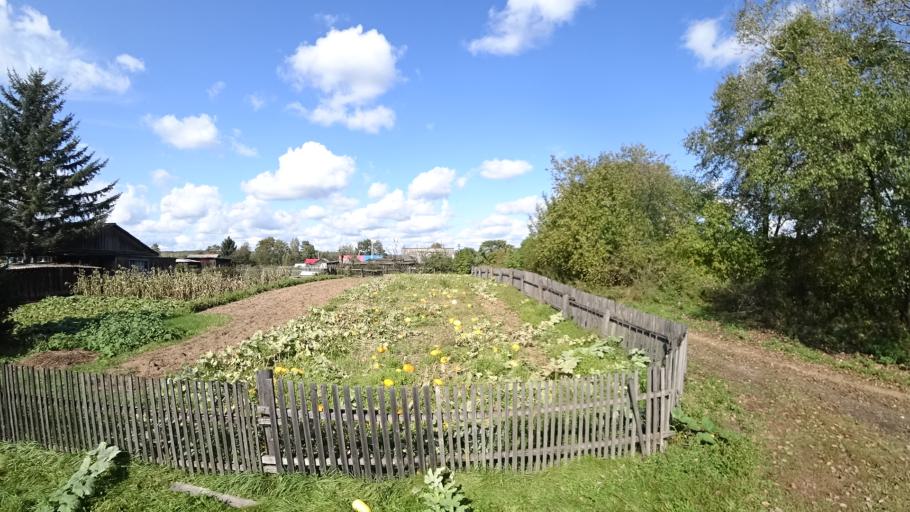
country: RU
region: Amur
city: Arkhara
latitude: 49.4030
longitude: 130.1556
